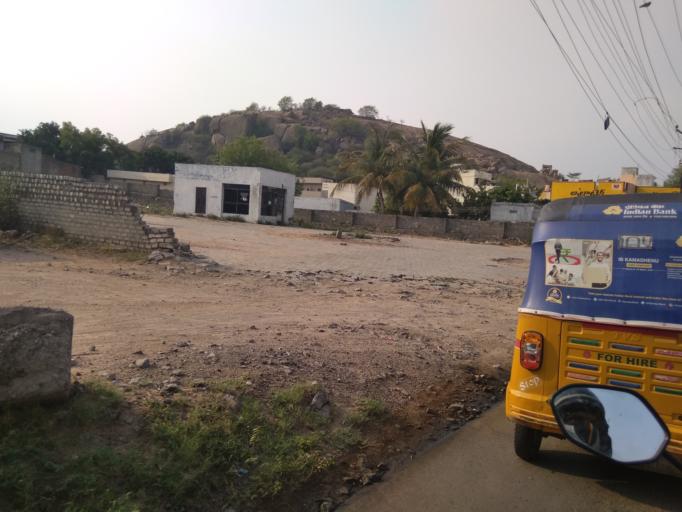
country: IN
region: Telangana
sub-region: Hyderabad
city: Malkajgiri
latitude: 17.4589
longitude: 78.5571
